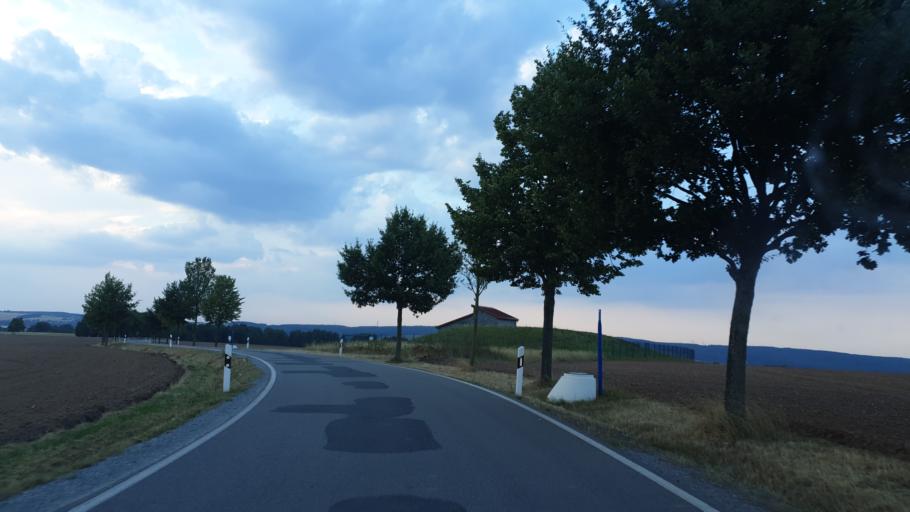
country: DE
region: Saxony
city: Niederdorf
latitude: 50.7841
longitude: 12.8049
